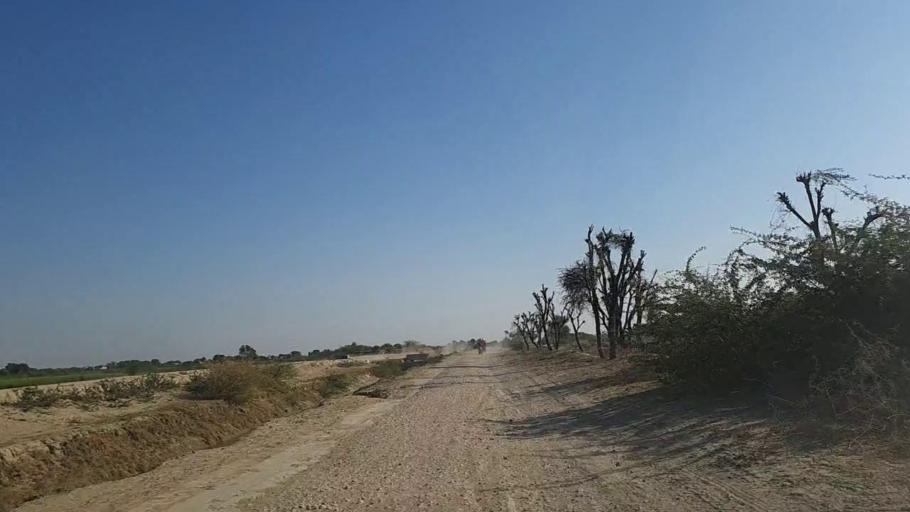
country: PK
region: Sindh
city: Naukot
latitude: 24.9528
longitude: 69.3226
